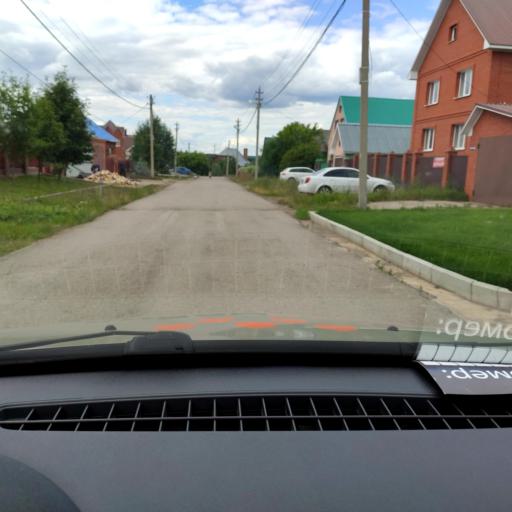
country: RU
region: Bashkortostan
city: Ufa
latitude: 54.6030
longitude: 55.9306
